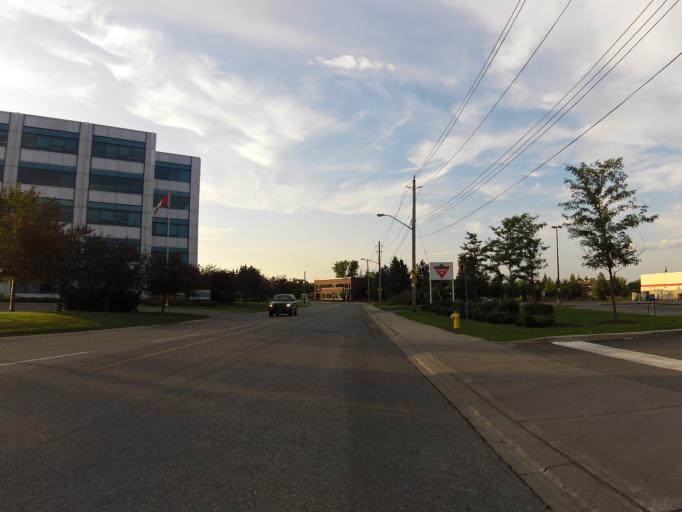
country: CA
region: Ontario
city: Bells Corners
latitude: 45.3212
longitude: -75.8371
